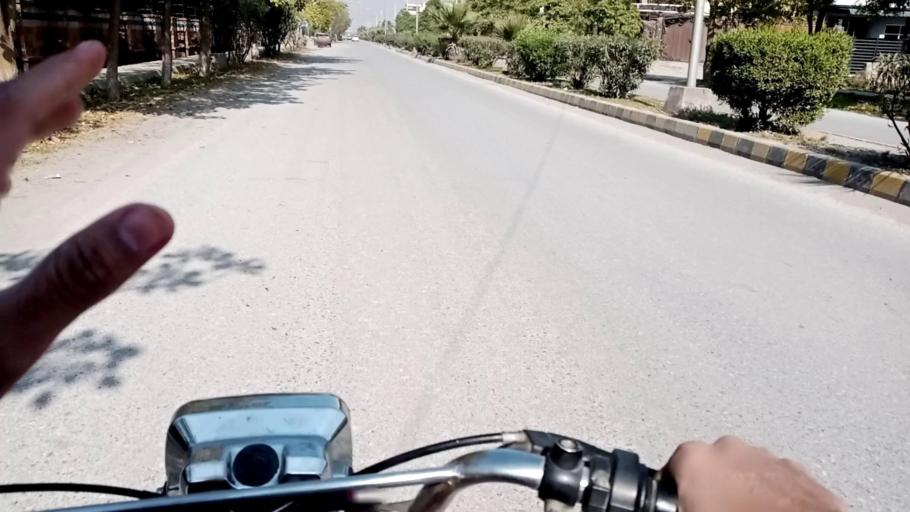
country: PK
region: Khyber Pakhtunkhwa
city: Peshawar
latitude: 33.9583
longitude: 71.4175
